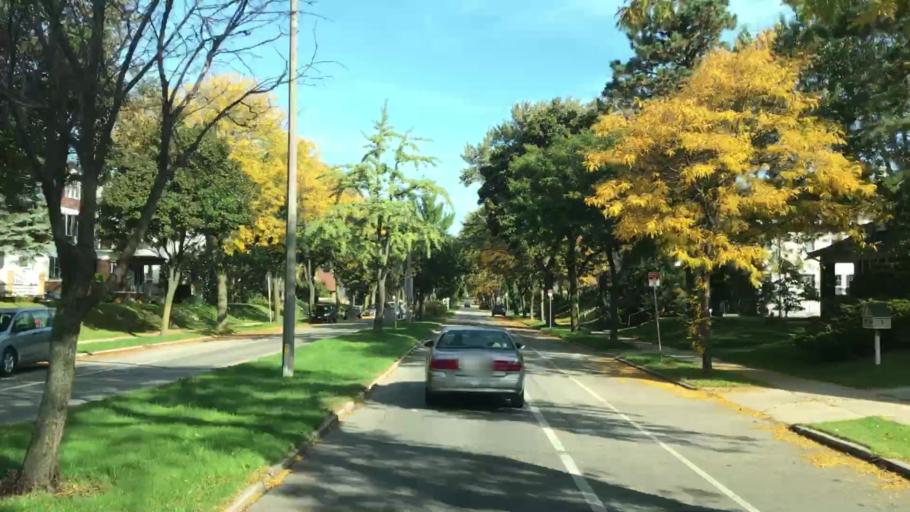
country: US
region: Wisconsin
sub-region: Milwaukee County
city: Shorewood
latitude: 43.0751
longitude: -87.8977
